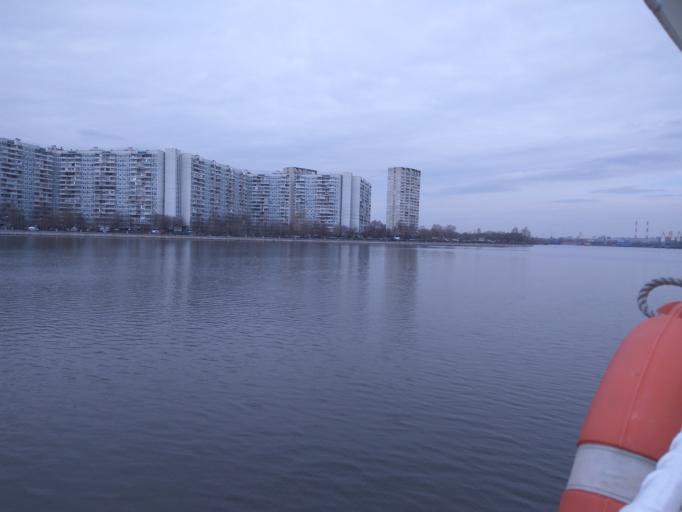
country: RU
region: Moscow
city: Mar'ino
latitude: 55.6807
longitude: 37.7129
